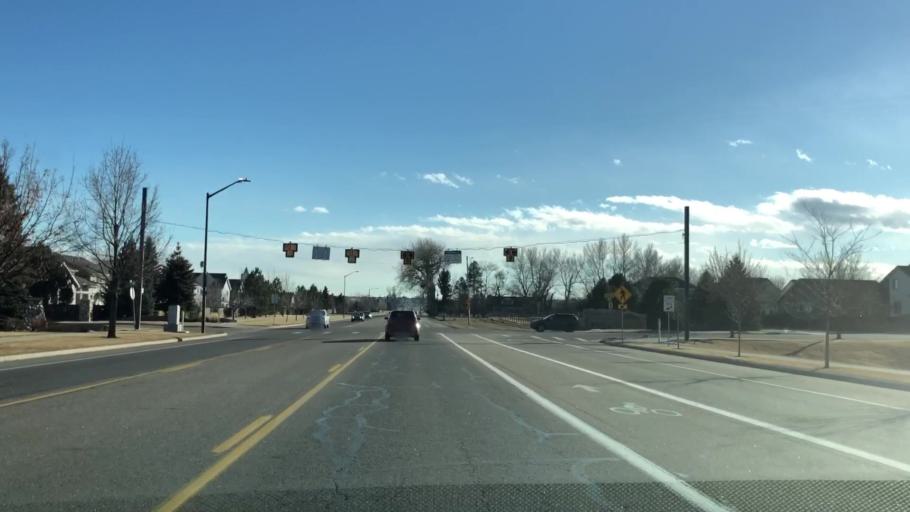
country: US
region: Colorado
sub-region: Larimer County
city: Fort Collins
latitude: 40.5000
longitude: -105.0393
